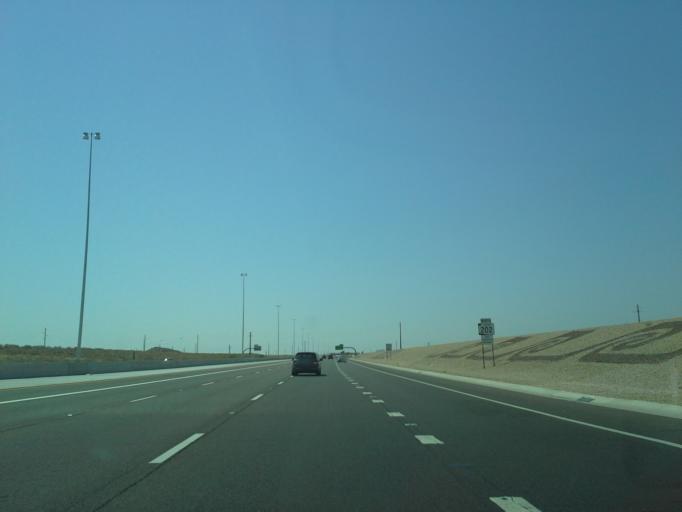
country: US
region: Arizona
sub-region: Pinal County
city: Apache Junction
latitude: 33.4414
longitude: -111.6574
